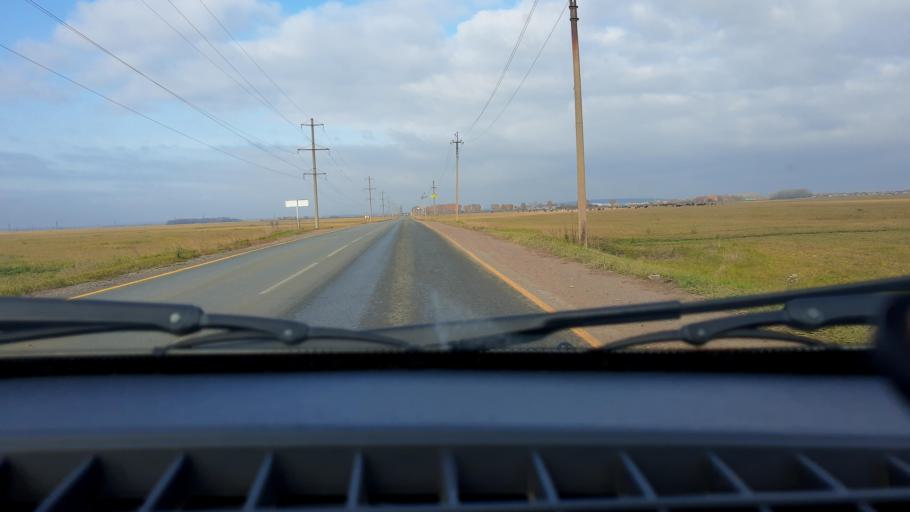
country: RU
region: Bashkortostan
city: Kabakovo
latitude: 54.5370
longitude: 56.0698
